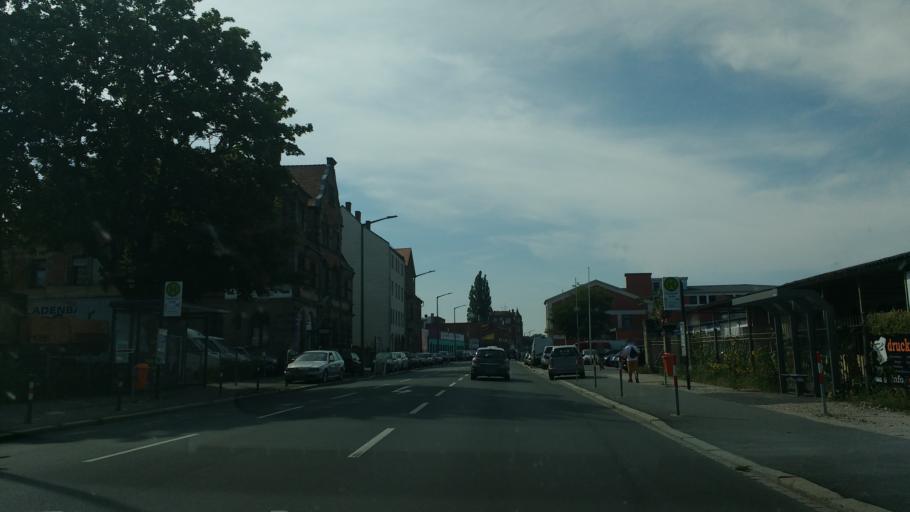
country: DE
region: Bavaria
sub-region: Regierungsbezirk Mittelfranken
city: Grossreuth bei Schweinau
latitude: 49.4588
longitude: 11.0106
